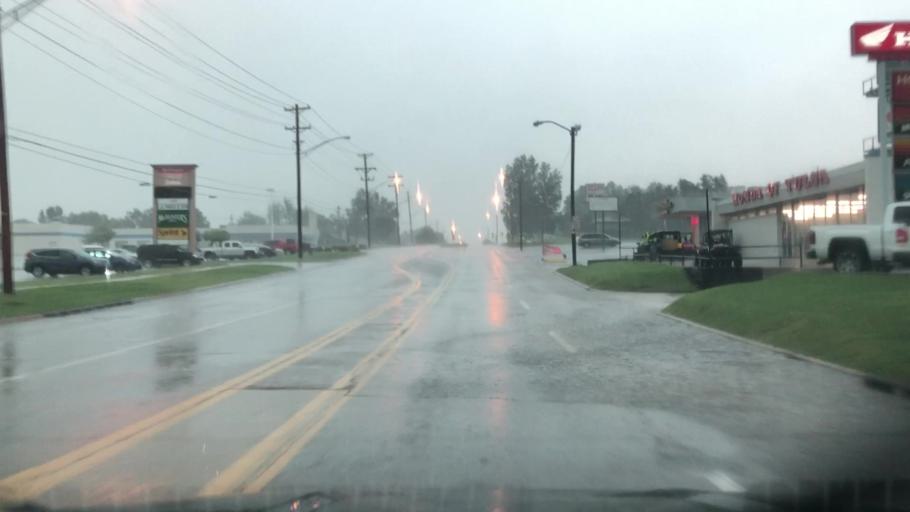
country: US
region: Oklahoma
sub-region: Tulsa County
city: Tulsa
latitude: 36.1333
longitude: -95.9216
